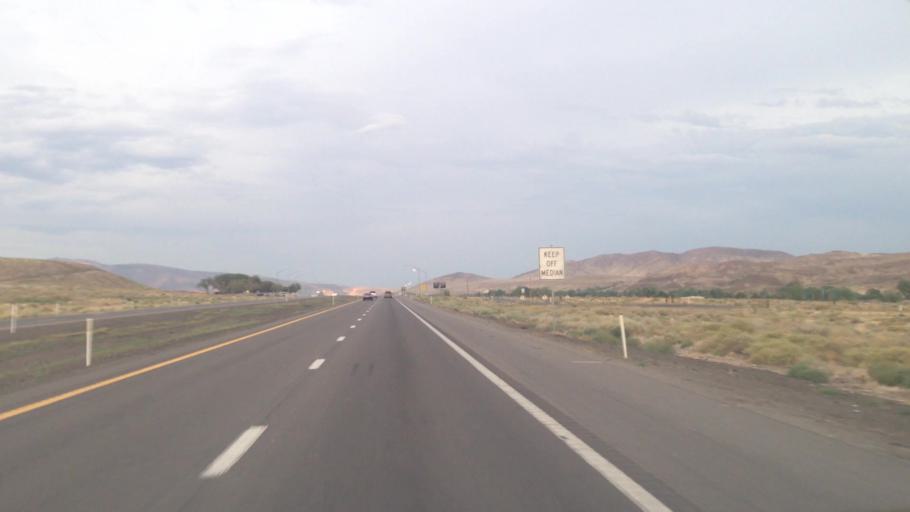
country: US
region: Nevada
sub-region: Lyon County
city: Fernley
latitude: 39.6000
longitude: -119.3435
